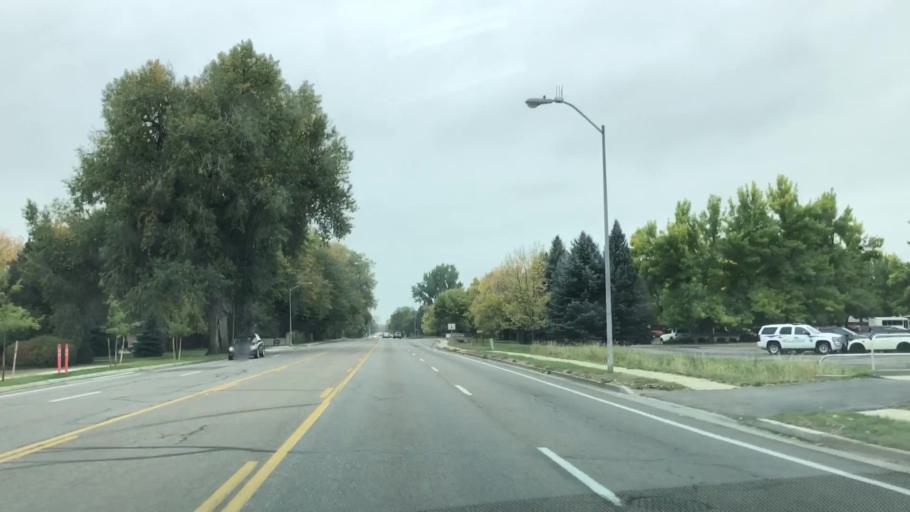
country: US
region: Colorado
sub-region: Larimer County
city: Fort Collins
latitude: 40.5594
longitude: -105.0580
